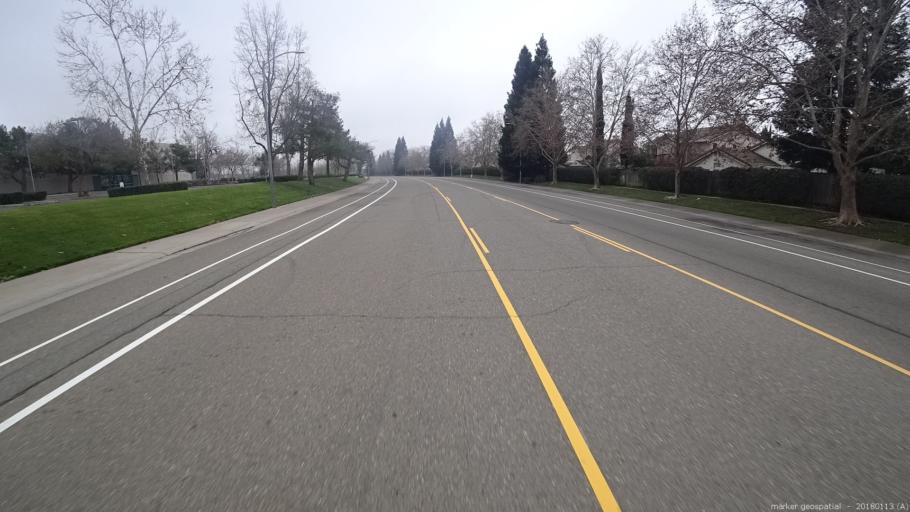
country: US
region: California
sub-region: Sacramento County
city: Rancho Cordova
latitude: 38.5812
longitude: -121.2916
